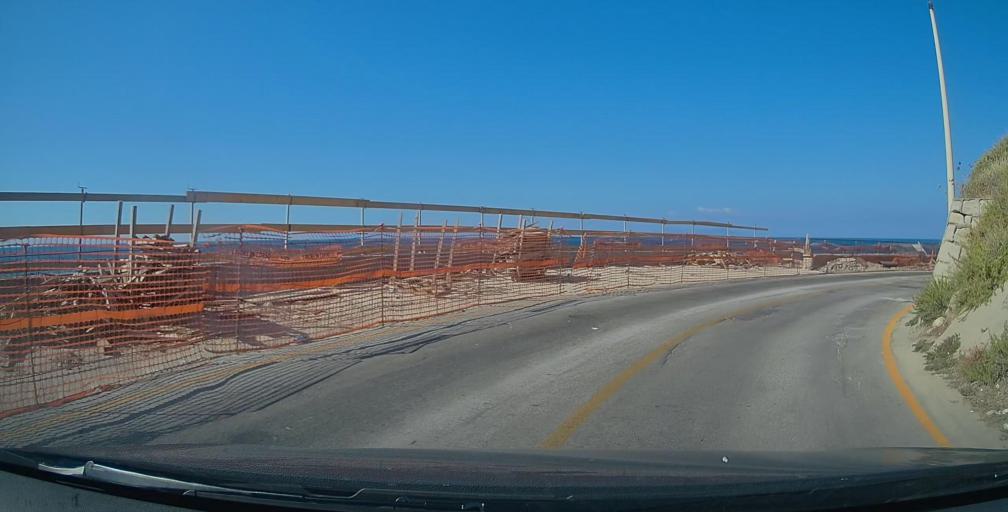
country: IT
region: Sicily
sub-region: Messina
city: Capo d'Orlando
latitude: 38.1649
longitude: 14.7467
